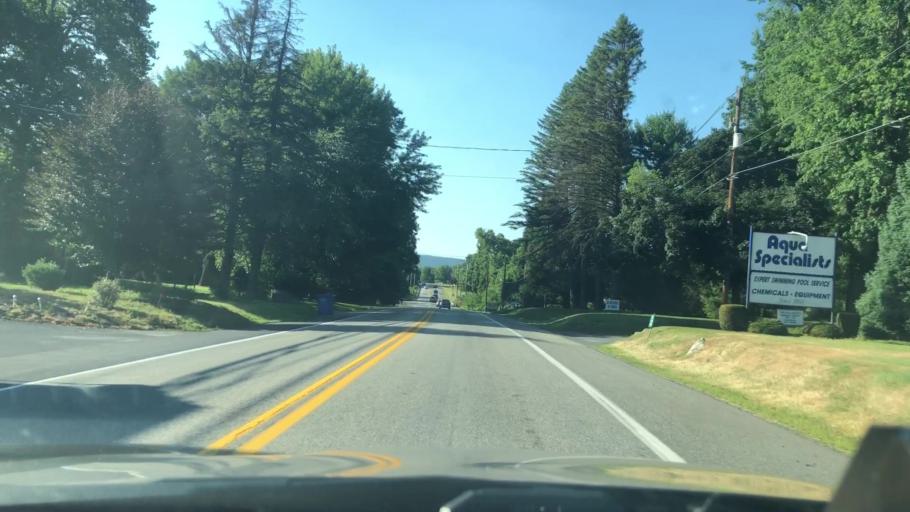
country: US
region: Pennsylvania
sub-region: Cumberland County
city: Mechanicsburg
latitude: 40.2349
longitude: -77.0066
